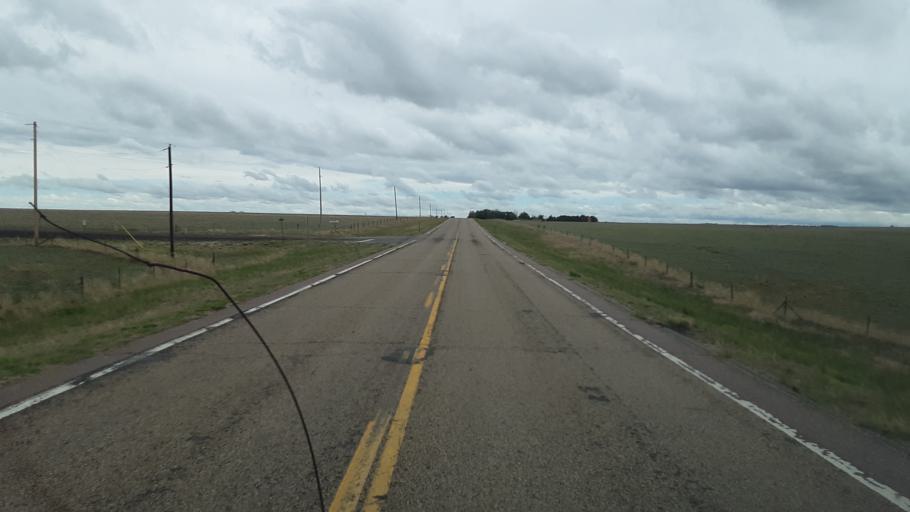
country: US
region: Colorado
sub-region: El Paso County
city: Ellicott
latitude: 38.8398
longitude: -104.0394
